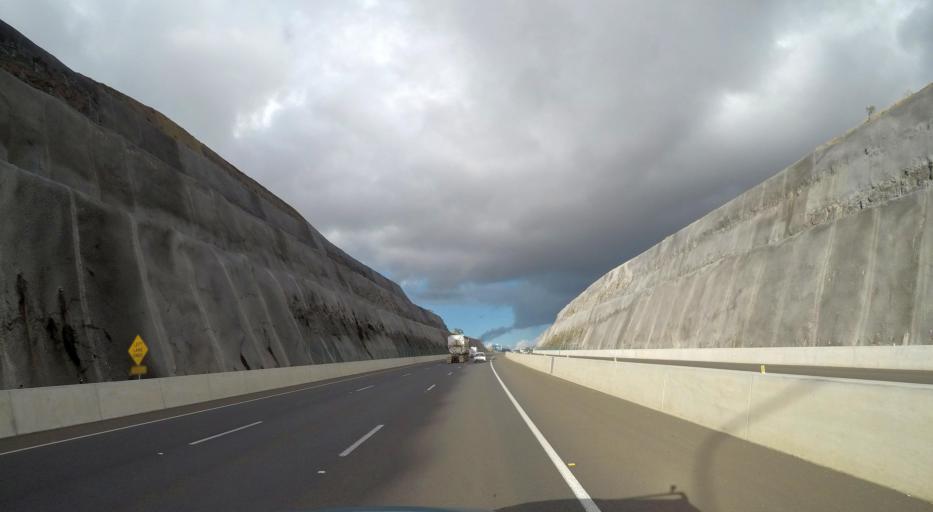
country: AU
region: Queensland
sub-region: Toowoomba
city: Wilsonton Heights
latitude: -27.5067
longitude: 151.9152
